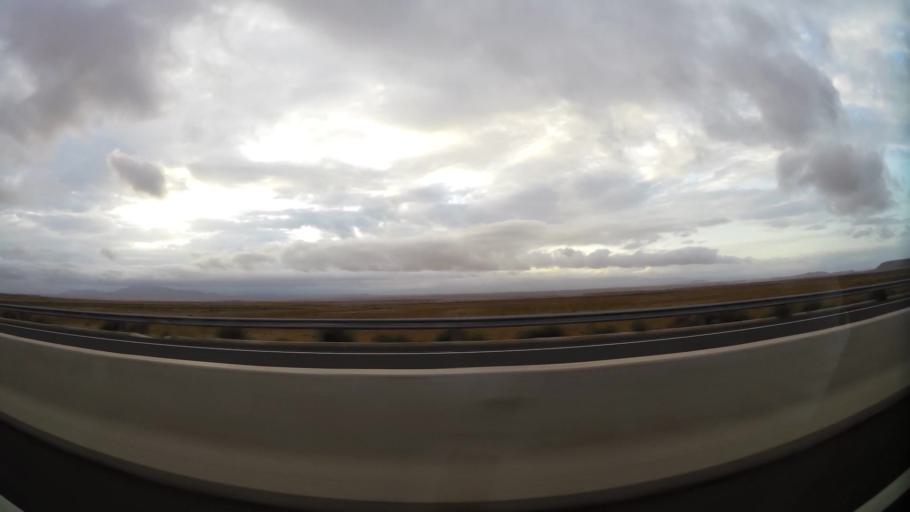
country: MA
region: Oriental
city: Taourirt
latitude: 34.4236
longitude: -3.1061
